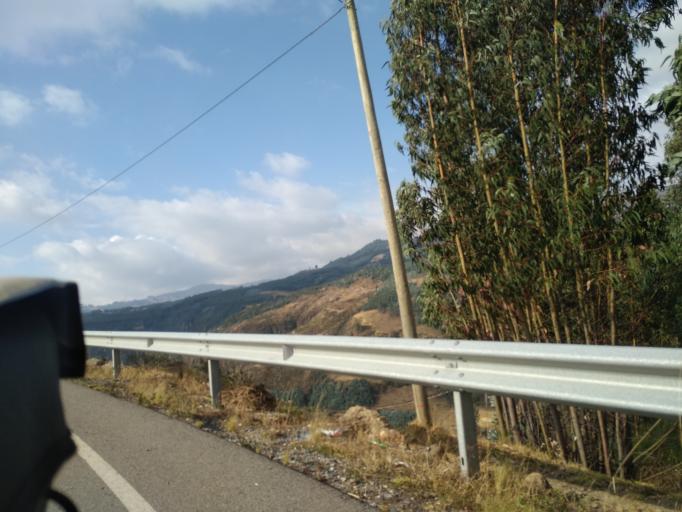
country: PE
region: La Libertad
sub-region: Provincia de Otuzco
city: Agallpampa
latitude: -7.9914
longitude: -78.5295
